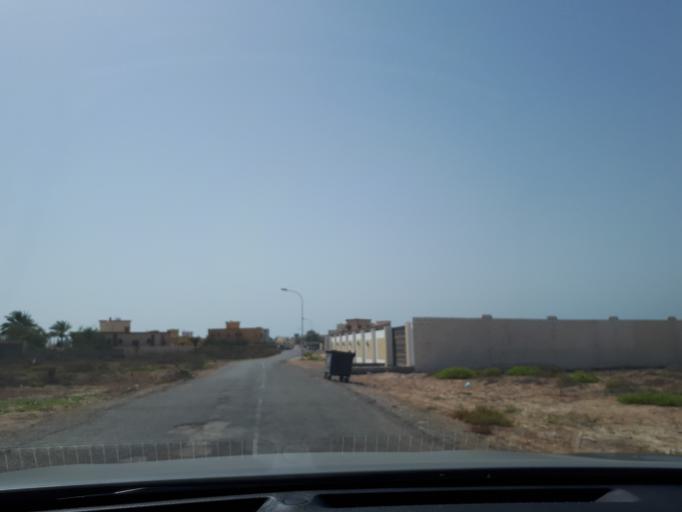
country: OM
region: Al Batinah
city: Barka'
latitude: 23.7024
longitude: 57.9399
